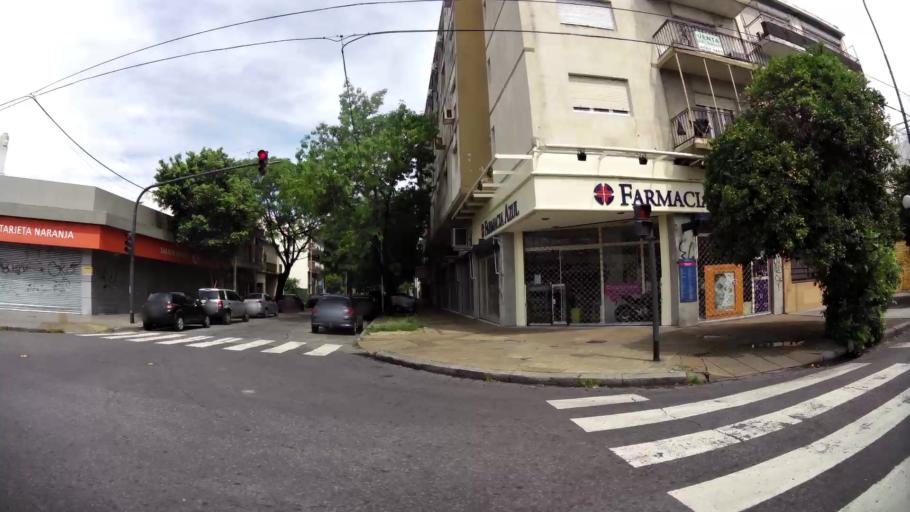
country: AR
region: Buenos Aires
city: Caseros
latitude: -34.6149
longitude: -58.5263
